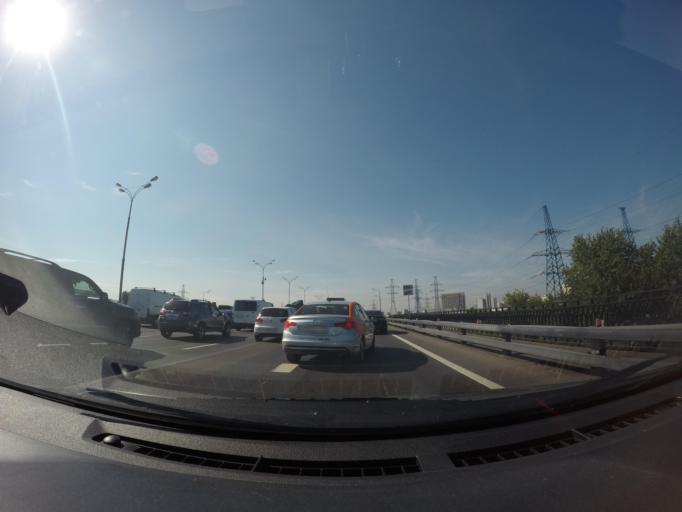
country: RU
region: Moscow
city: Zhulebino
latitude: 55.7099
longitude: 37.8357
